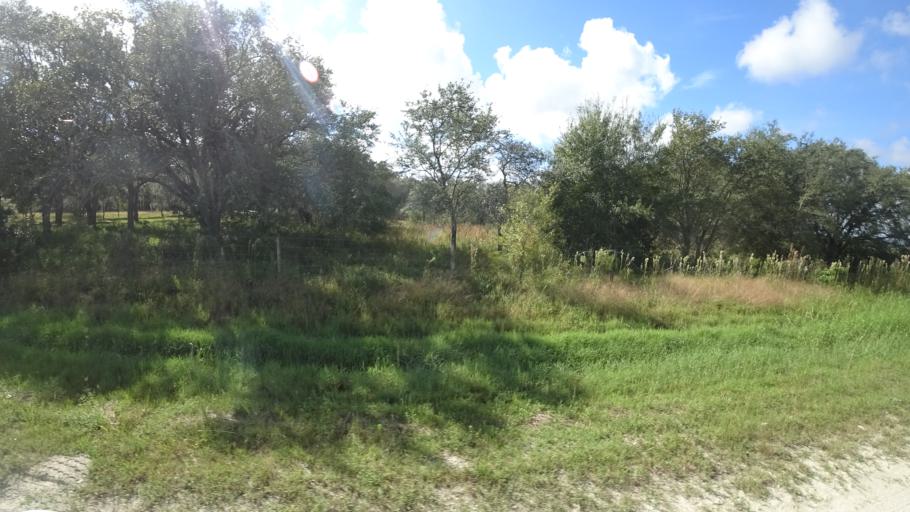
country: US
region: Florida
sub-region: Sarasota County
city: Lake Sarasota
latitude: 27.3250
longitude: -82.2191
